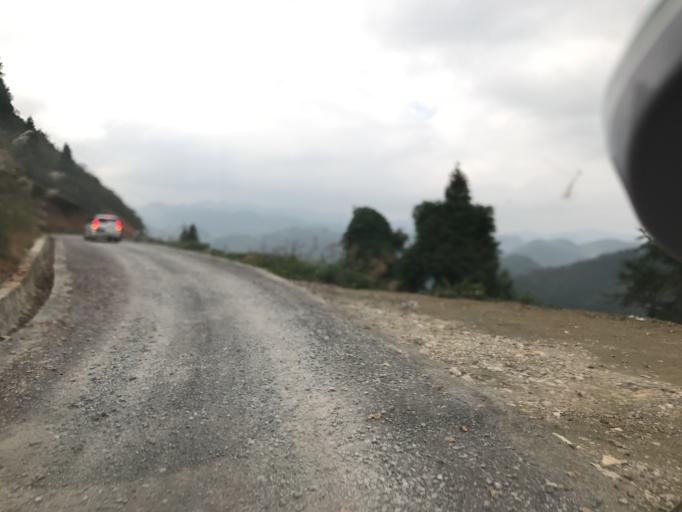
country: CN
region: Guizhou Sheng
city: Donghua
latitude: 28.0609
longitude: 108.1058
